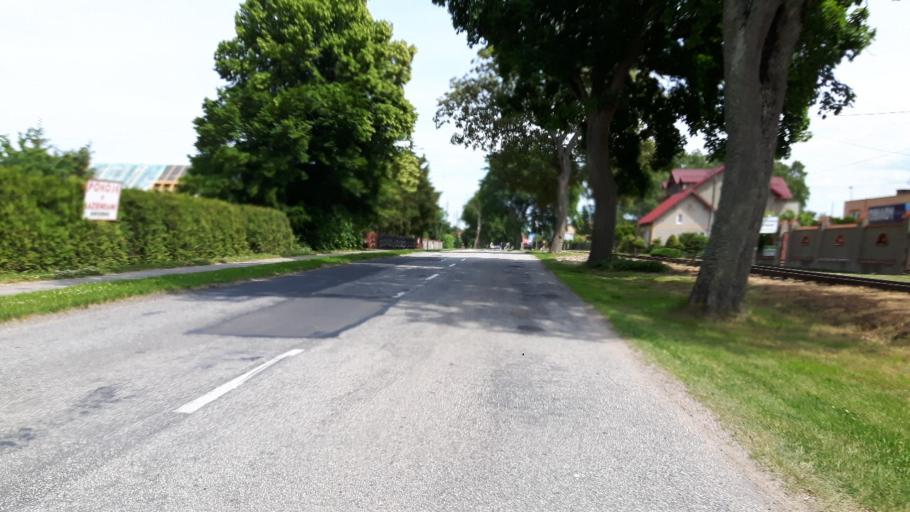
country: PL
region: Pomeranian Voivodeship
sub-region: Powiat nowodworski
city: Stegna
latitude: 54.3332
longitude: 19.0396
